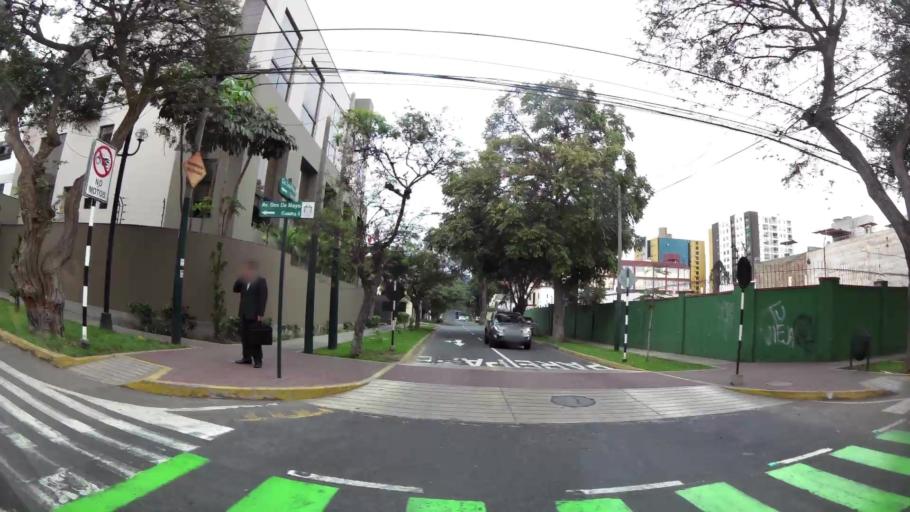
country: PE
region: Lima
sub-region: Lima
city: San Isidro
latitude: -12.0912
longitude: -77.0372
